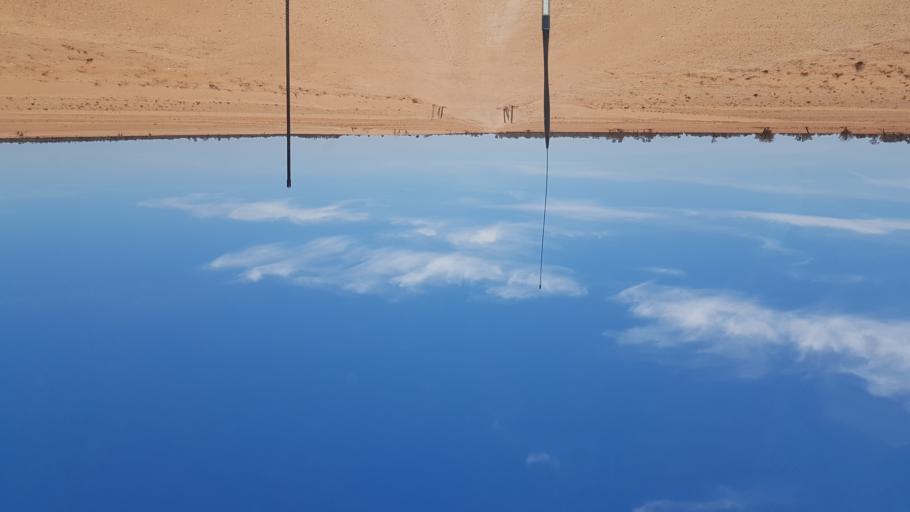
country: AU
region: New South Wales
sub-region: Wentworth
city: Dareton
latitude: -33.3515
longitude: 141.4654
